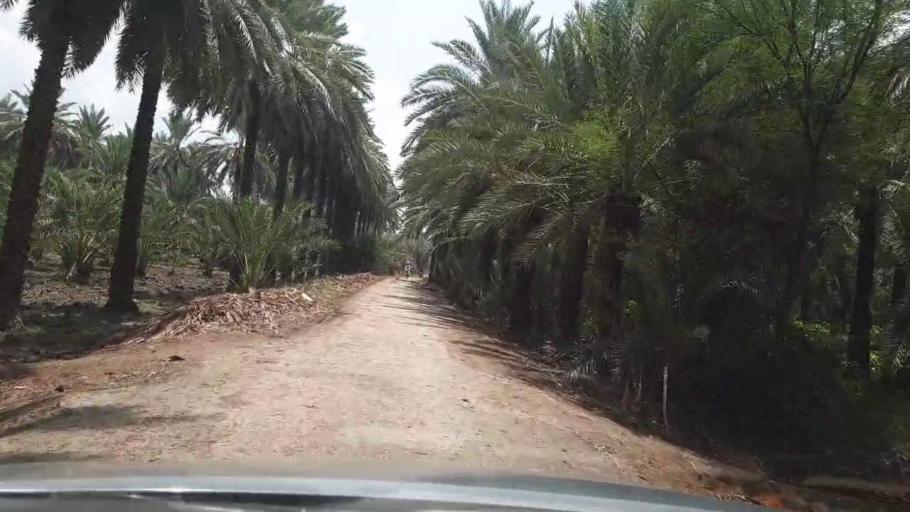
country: PK
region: Sindh
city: Khairpur
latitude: 27.6343
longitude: 68.7320
